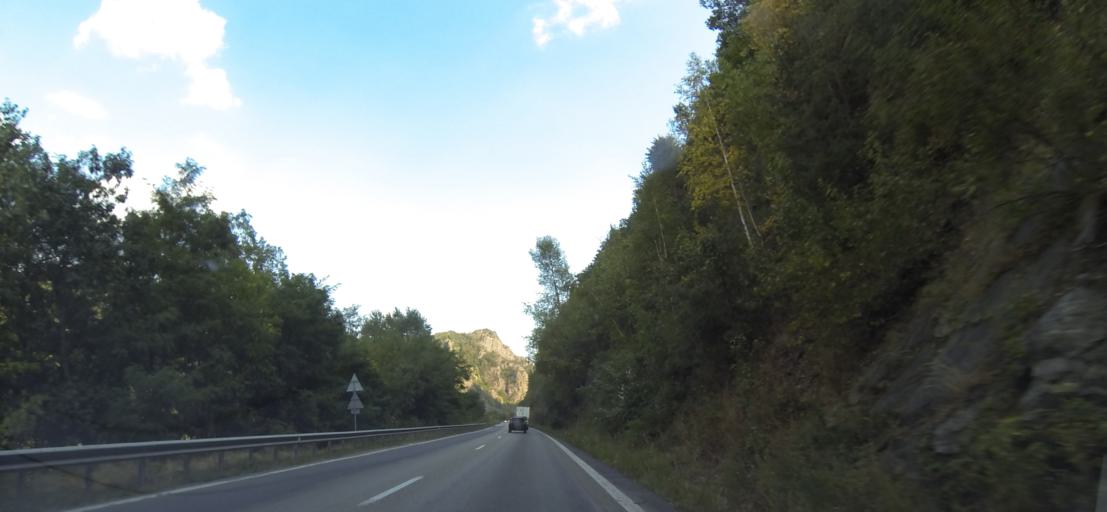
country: RO
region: Valcea
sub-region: Oras Calimanesti
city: Calimanesti
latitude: 45.2887
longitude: 24.2982
